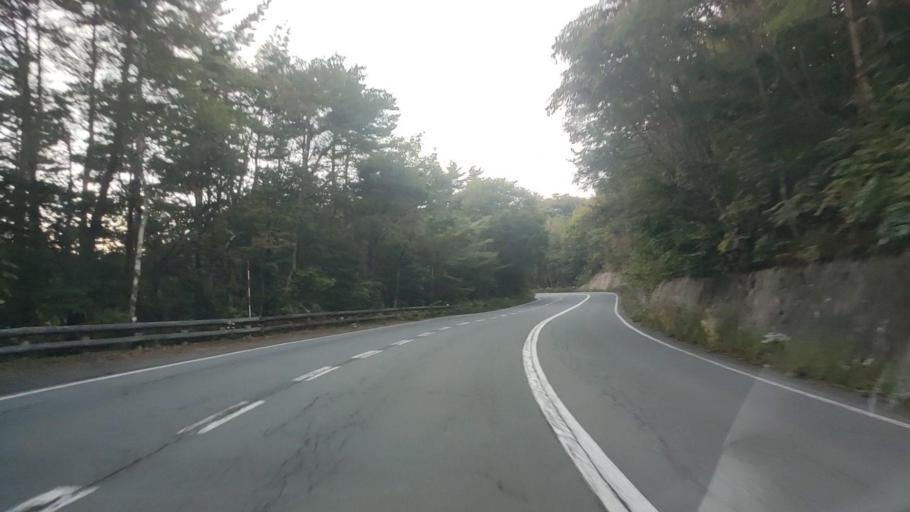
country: JP
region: Nagano
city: Komoro
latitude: 36.3898
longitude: 138.5844
